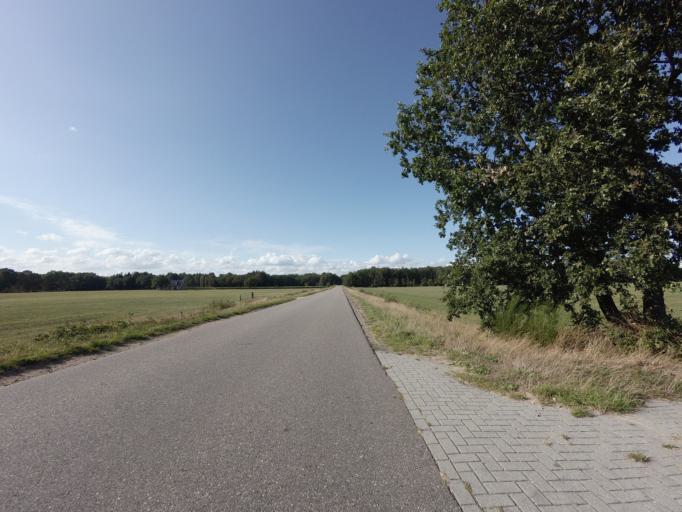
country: NL
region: Friesland
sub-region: Gemeente Heerenveen
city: Jubbega
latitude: 52.9789
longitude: 6.1838
